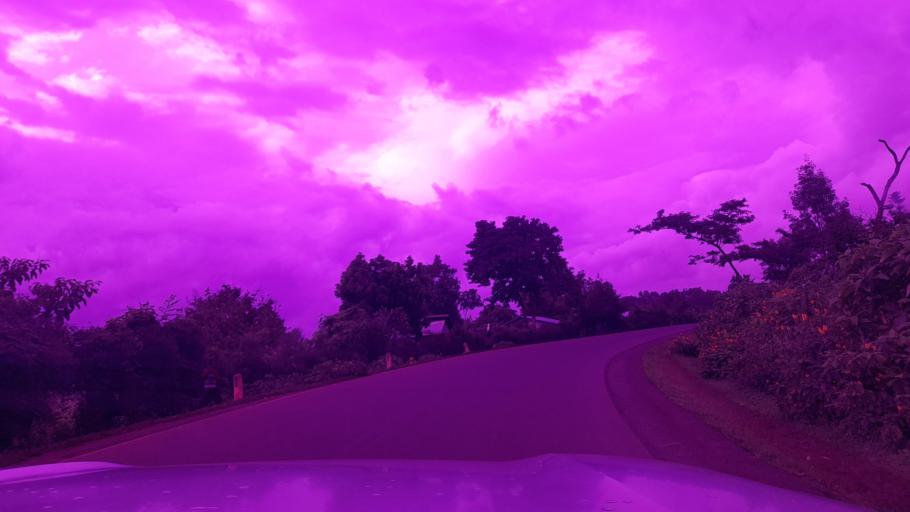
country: ET
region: Oromiya
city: Jima
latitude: 7.8994
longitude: 37.3881
